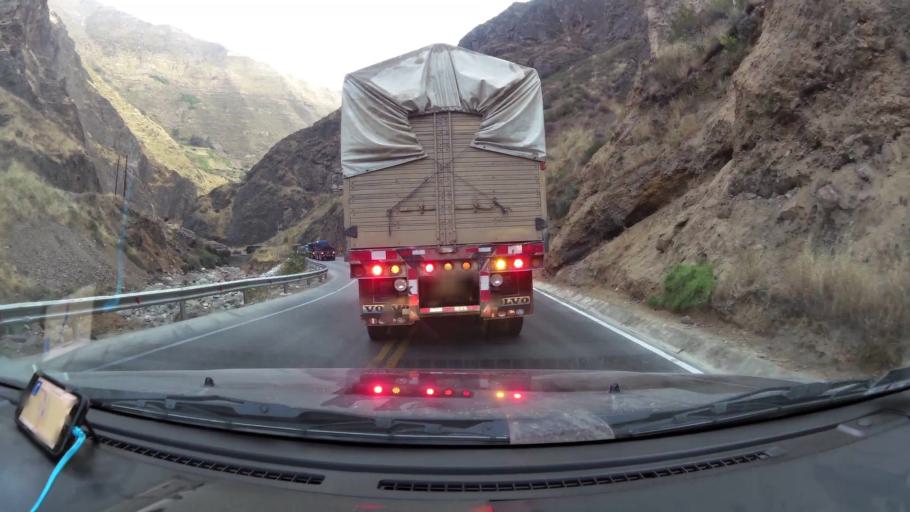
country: PE
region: Lima
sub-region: Provincia de Huarochiri
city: San Mateo
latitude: -11.8063
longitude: -76.3419
